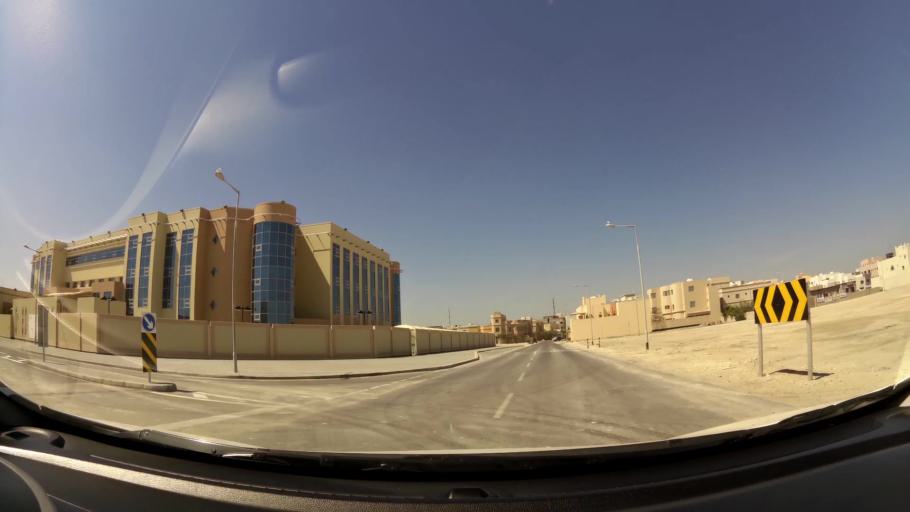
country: BH
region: Muharraq
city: Al Muharraq
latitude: 26.2784
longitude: 50.6005
